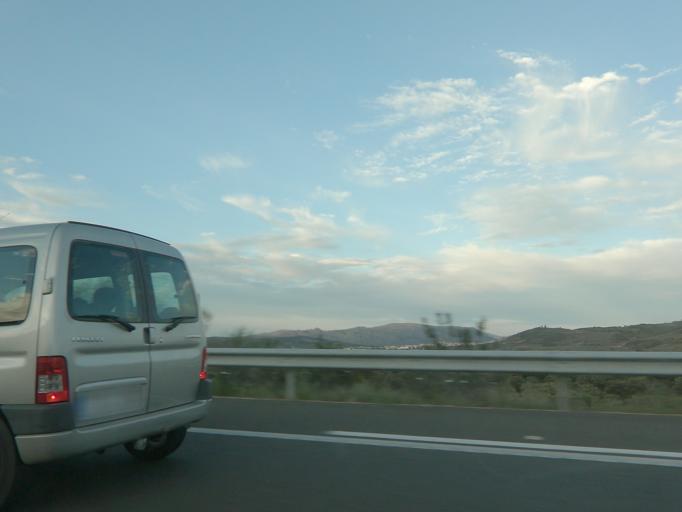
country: ES
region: Extremadura
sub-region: Provincia de Caceres
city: Alcuescar
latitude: 39.1714
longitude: -6.2704
